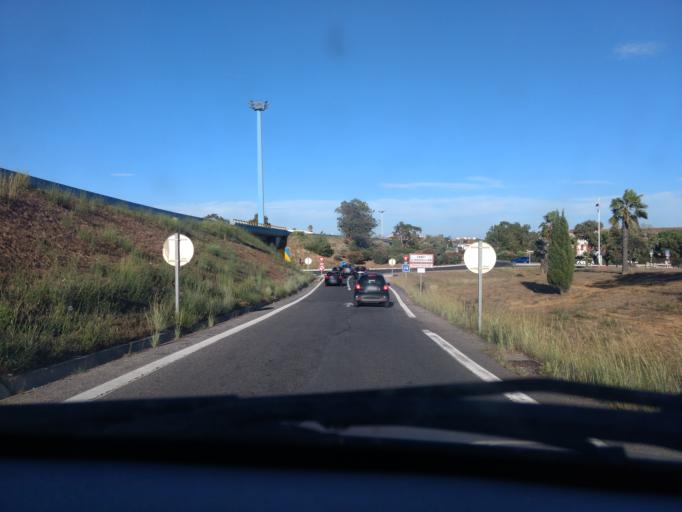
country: FR
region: Languedoc-Roussillon
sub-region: Departement des Pyrenees-Orientales
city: Canet-en-Roussillon
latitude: 42.7025
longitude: 3.0140
